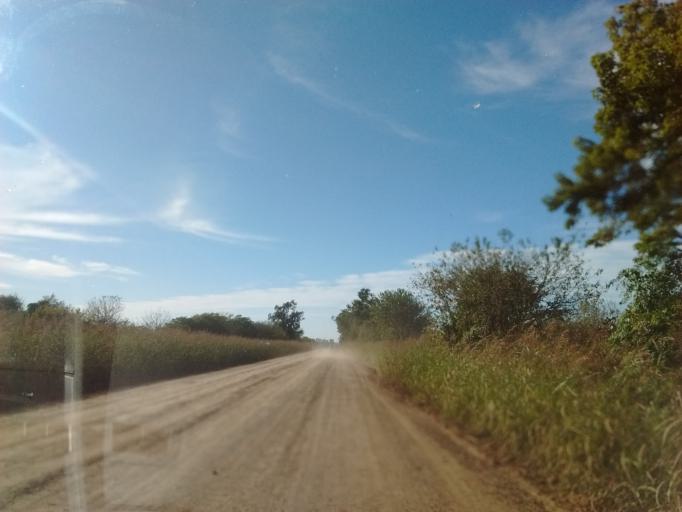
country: AR
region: Santa Fe
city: Coronda
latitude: -32.2296
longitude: -60.9719
